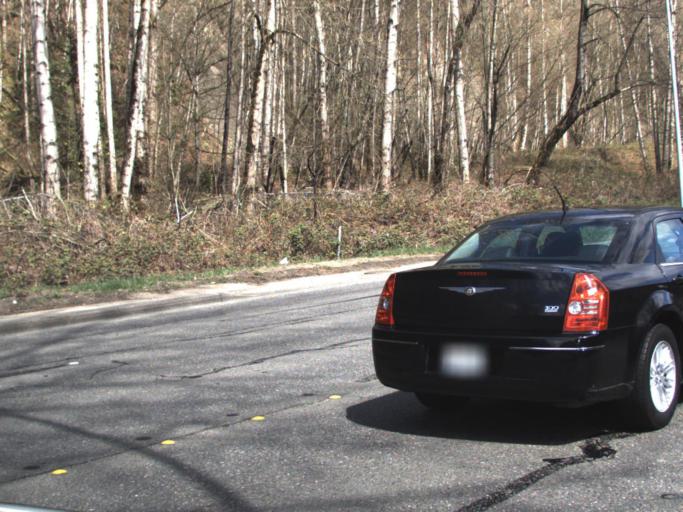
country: US
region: Washington
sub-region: King County
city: Renton
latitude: 47.4774
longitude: -122.1818
